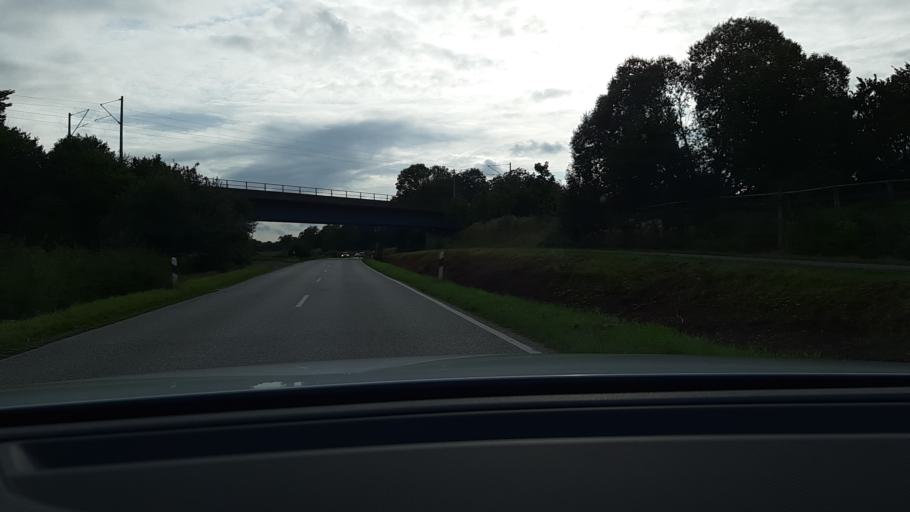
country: DE
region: Schleswig-Holstein
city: Wesenberg
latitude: 53.8347
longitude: 10.5470
